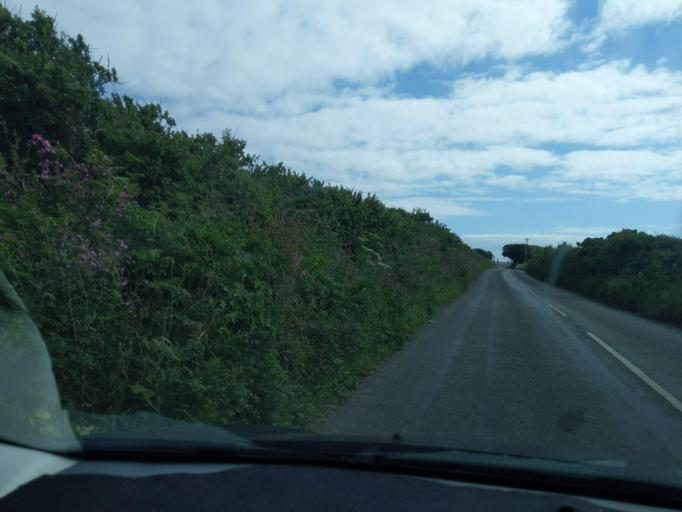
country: GB
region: England
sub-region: Cornwall
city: St. Buryan
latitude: 50.0786
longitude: -5.6186
